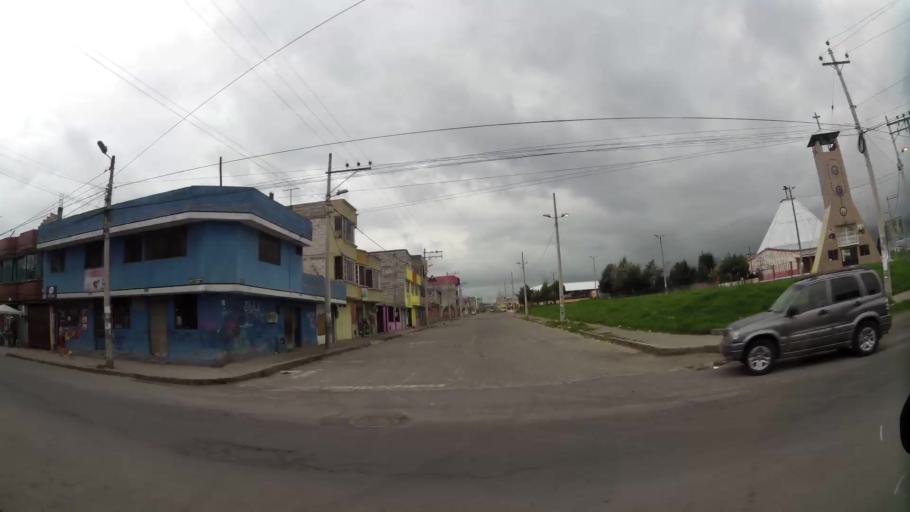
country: EC
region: Pichincha
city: Sangolqui
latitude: -0.3285
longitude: -78.5363
